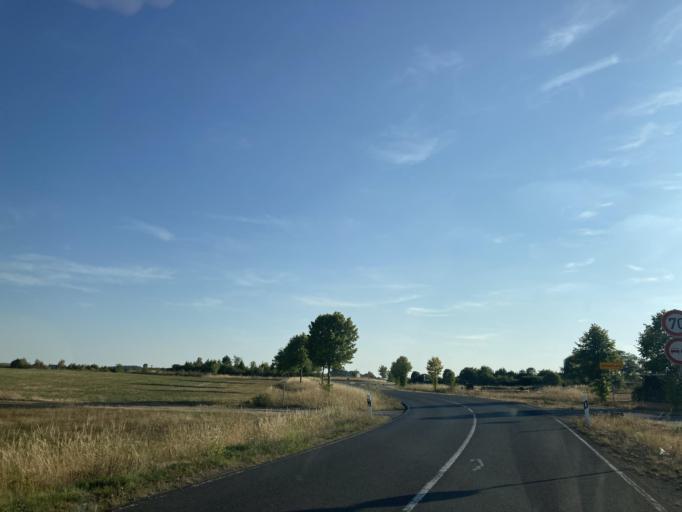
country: DE
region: Hesse
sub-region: Regierungsbezirk Kassel
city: Fulda
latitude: 50.5317
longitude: 9.6325
